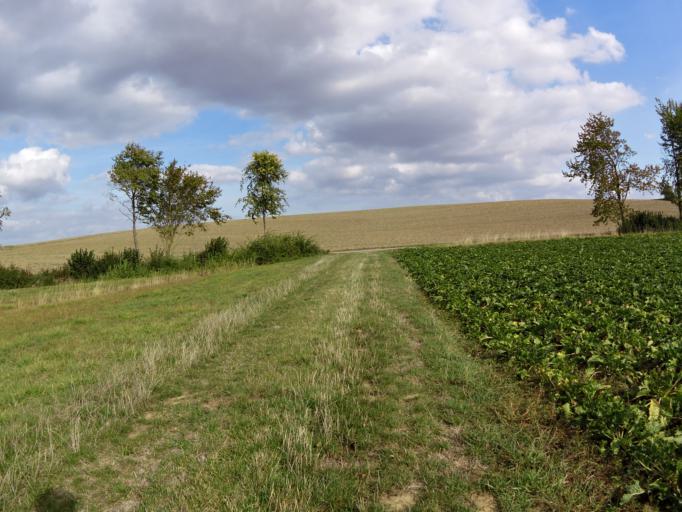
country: DE
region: Bavaria
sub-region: Regierungsbezirk Unterfranken
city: Giebelstadt
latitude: 49.6996
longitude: 9.9500
